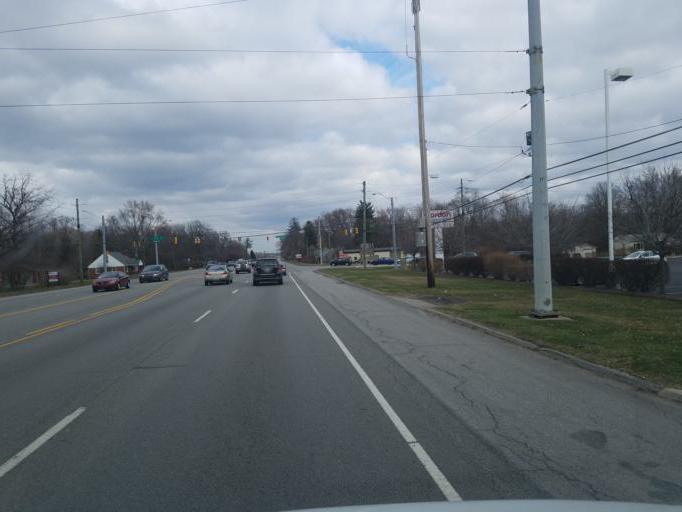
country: US
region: Indiana
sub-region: Marion County
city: Clermont
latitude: 39.7638
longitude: -86.3183
